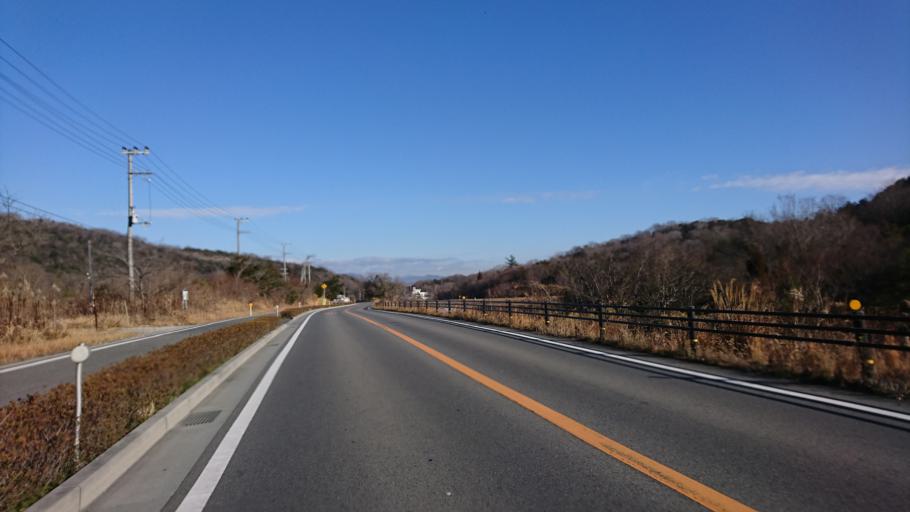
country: JP
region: Hyogo
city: Ono
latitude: 34.8420
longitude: 134.8775
